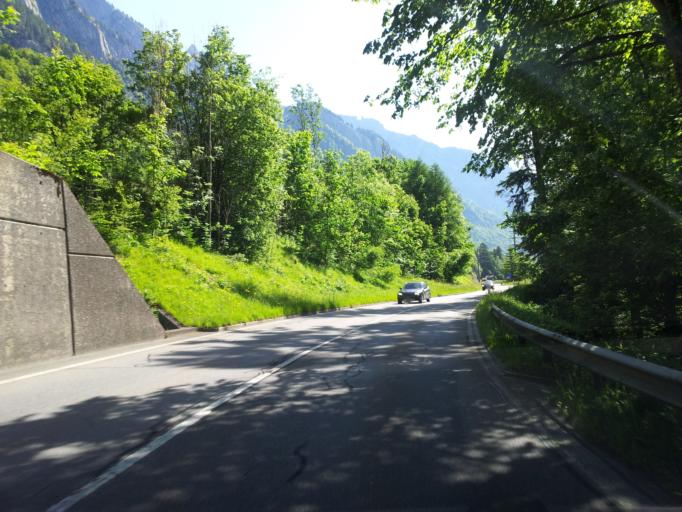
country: CH
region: Bern
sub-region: Interlaken-Oberhasli District
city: Lauterbrunnen
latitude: 46.6352
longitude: 7.9197
